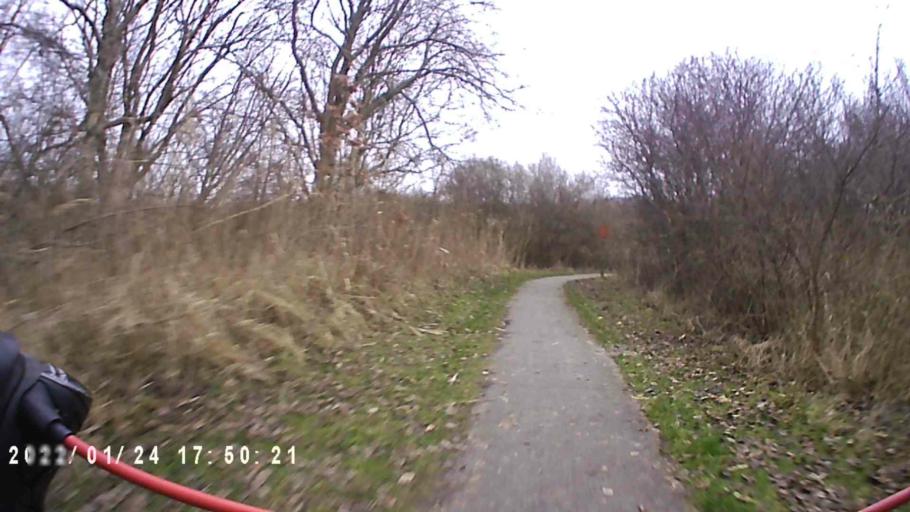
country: NL
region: Friesland
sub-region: Gemeente Schiermonnikoog
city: Schiermonnikoog
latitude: 53.4097
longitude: 6.2263
